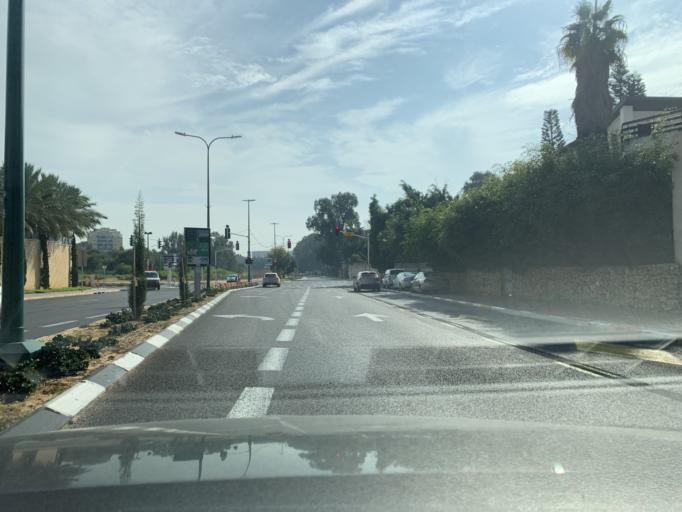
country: IL
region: Central District
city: Ganne Tiqwa
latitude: 32.0540
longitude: 34.8525
